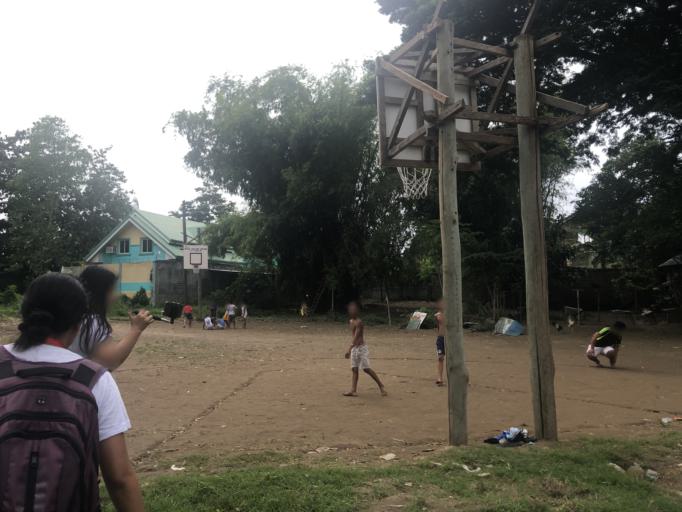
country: PH
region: Central Visayas
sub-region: Province of Negros Oriental
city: Dumaguete
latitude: 9.3041
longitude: 123.2985
